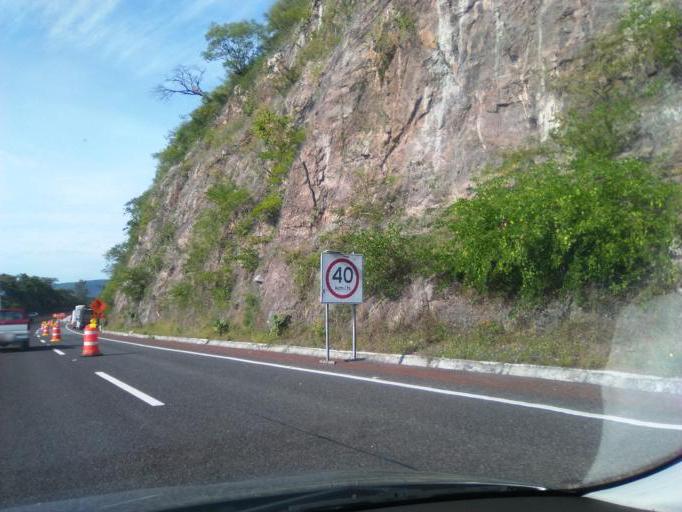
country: MX
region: Morelos
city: Tilzapotla
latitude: 18.4021
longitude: -99.1716
